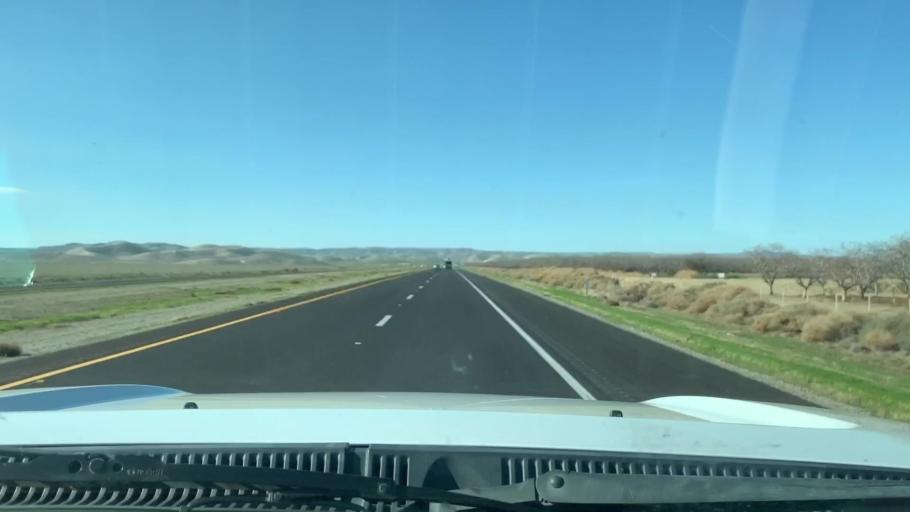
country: US
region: California
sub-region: Kern County
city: Lost Hills
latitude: 35.6146
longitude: -119.9385
